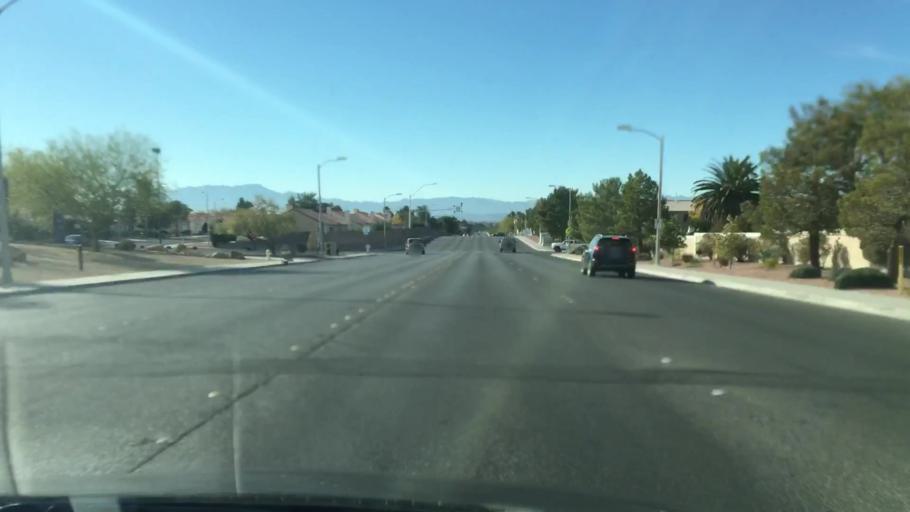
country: US
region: Nevada
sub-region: Clark County
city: Whitney
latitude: 36.0497
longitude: -115.1042
